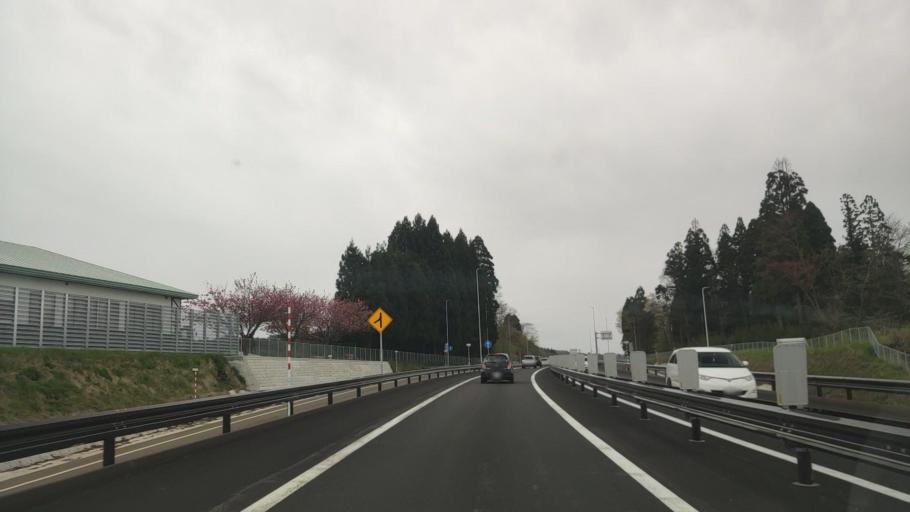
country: JP
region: Akita
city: Takanosu
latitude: 40.2070
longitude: 140.3326
